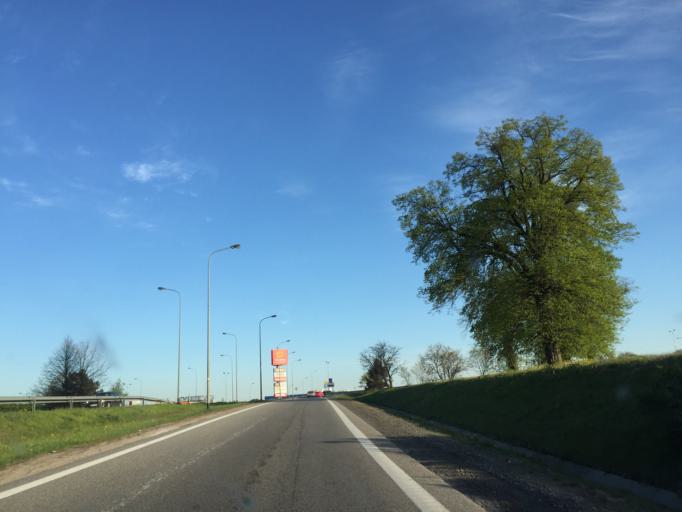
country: PL
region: Pomeranian Voivodeship
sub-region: Sopot
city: Sopot
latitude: 54.3779
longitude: 18.5146
